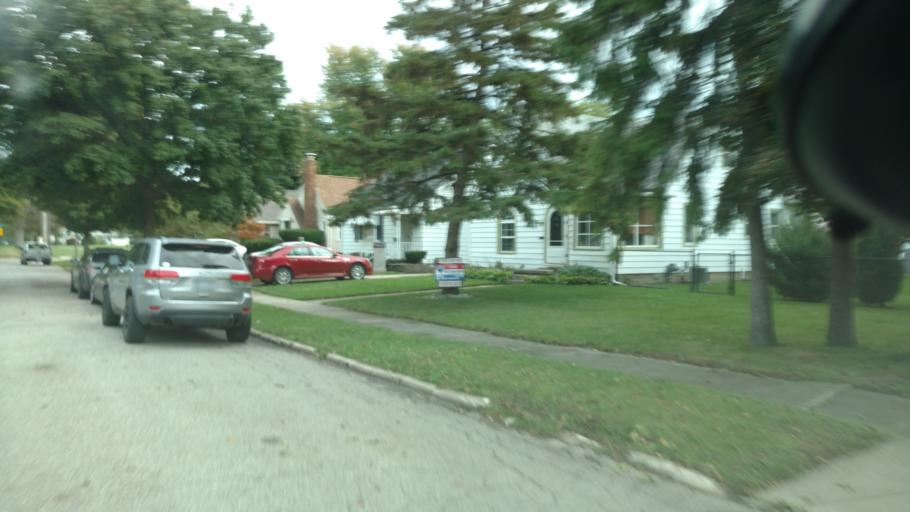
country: US
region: Michigan
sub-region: Ingham County
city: Edgemont Park
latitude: 42.7395
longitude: -84.5795
